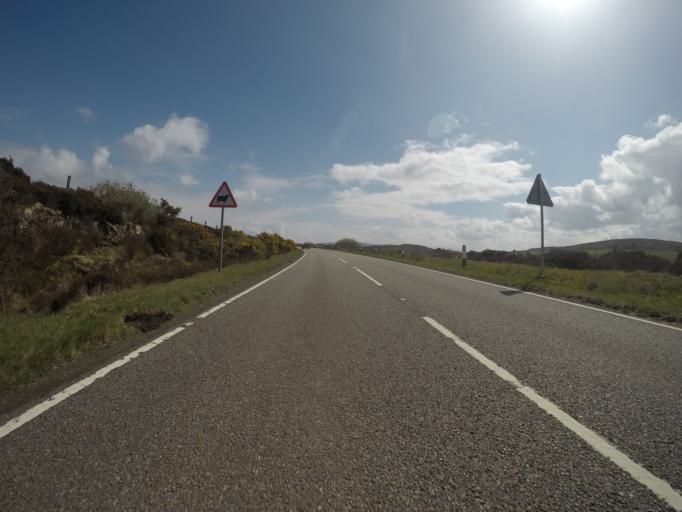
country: GB
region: Scotland
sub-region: Highland
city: Portree
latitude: 57.4747
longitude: -6.2989
